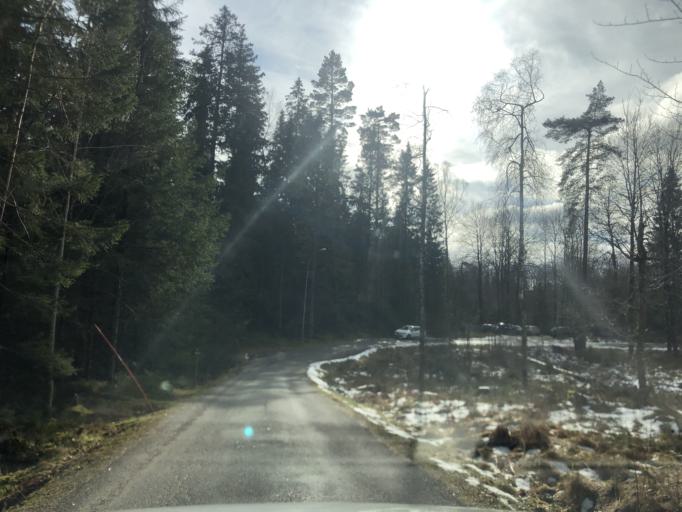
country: SE
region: Vaestra Goetaland
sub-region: Ulricehamns Kommun
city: Ulricehamn
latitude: 57.7823
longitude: 13.4399
